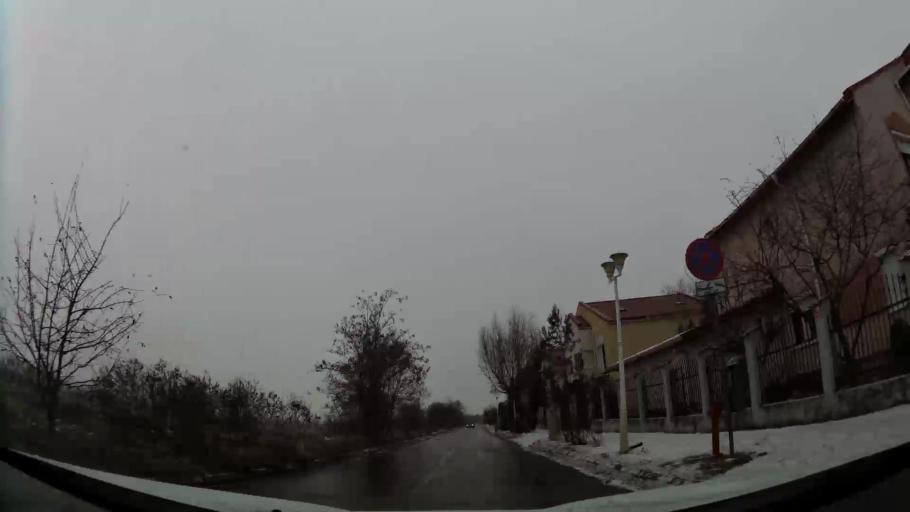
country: RO
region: Prahova
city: Ploiesti
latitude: 44.9611
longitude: 25.9994
